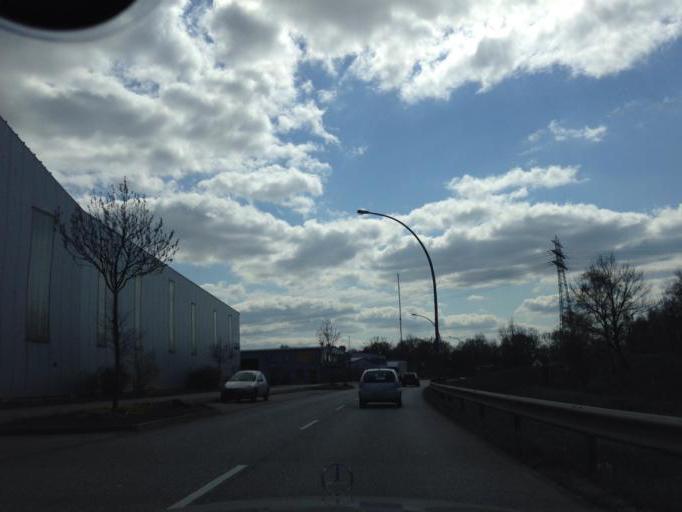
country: DE
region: Hamburg
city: Wandsbek
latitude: 53.5282
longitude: 10.1096
